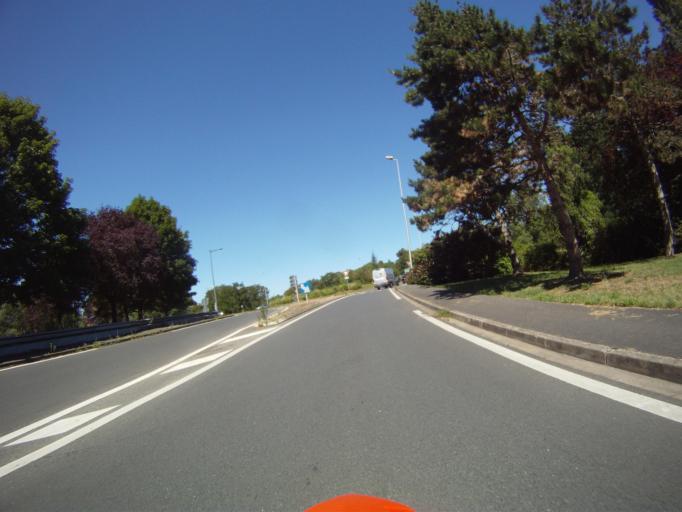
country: FR
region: Centre
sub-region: Departement d'Indre-et-Loire
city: Rochecorbon
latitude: 47.4188
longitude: 0.7478
